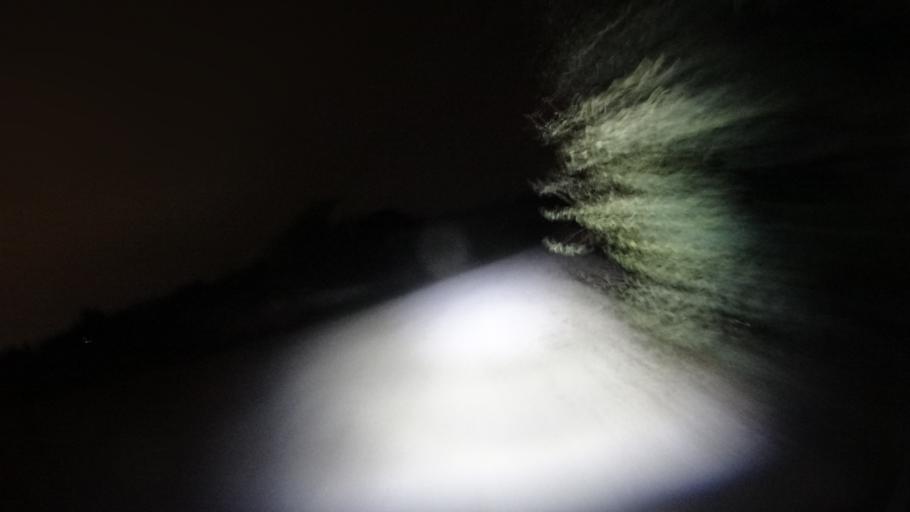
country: PL
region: Masovian Voivodeship
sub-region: Powiat warszawski zachodni
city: Ozarow Mazowiecki
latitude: 52.2443
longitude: 20.7856
